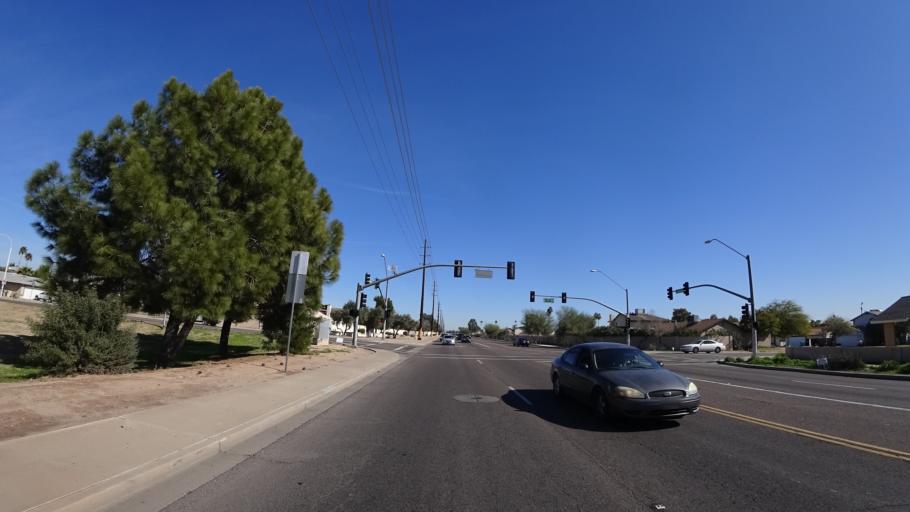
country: US
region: Arizona
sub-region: Maricopa County
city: Glendale
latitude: 33.5090
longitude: -112.2289
